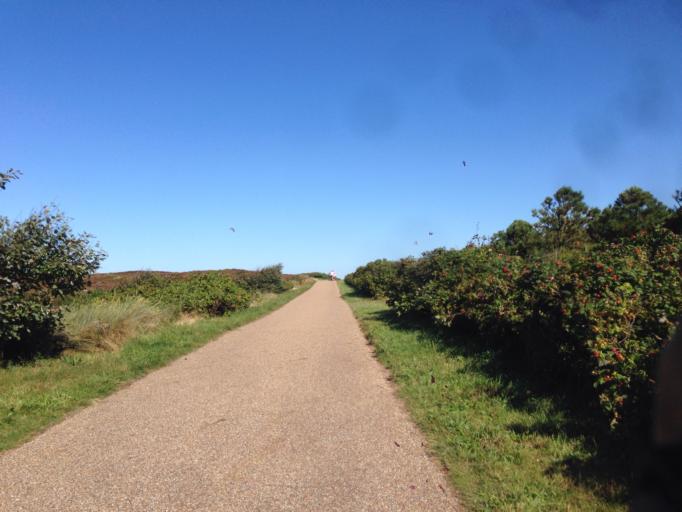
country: DE
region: Schleswig-Holstein
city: Tinnum
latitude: 54.9512
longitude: 8.3369
